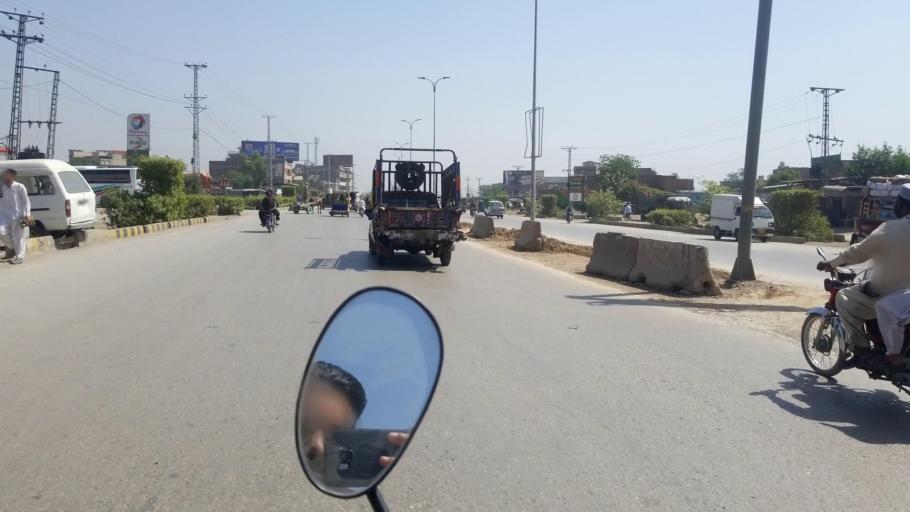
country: PK
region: Khyber Pakhtunkhwa
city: Peshawar
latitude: 33.9822
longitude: 71.5681
